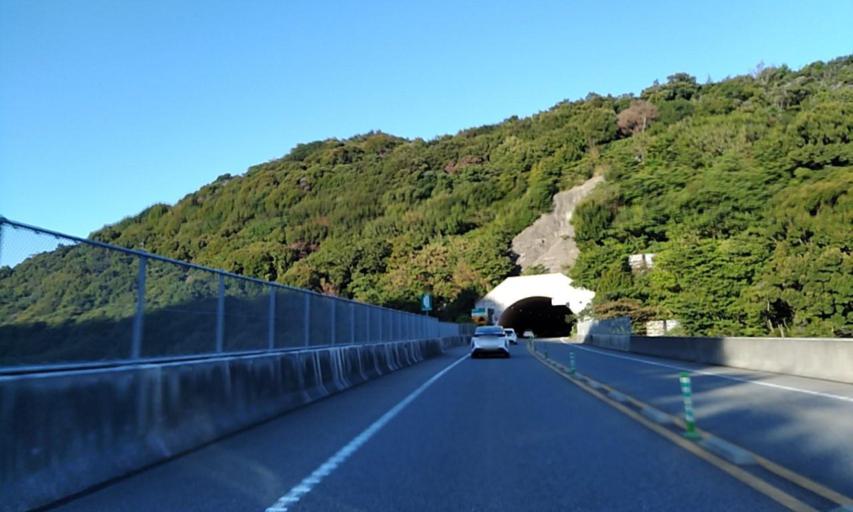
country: JP
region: Wakayama
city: Wakayama-shi
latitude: 34.3227
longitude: 135.1983
